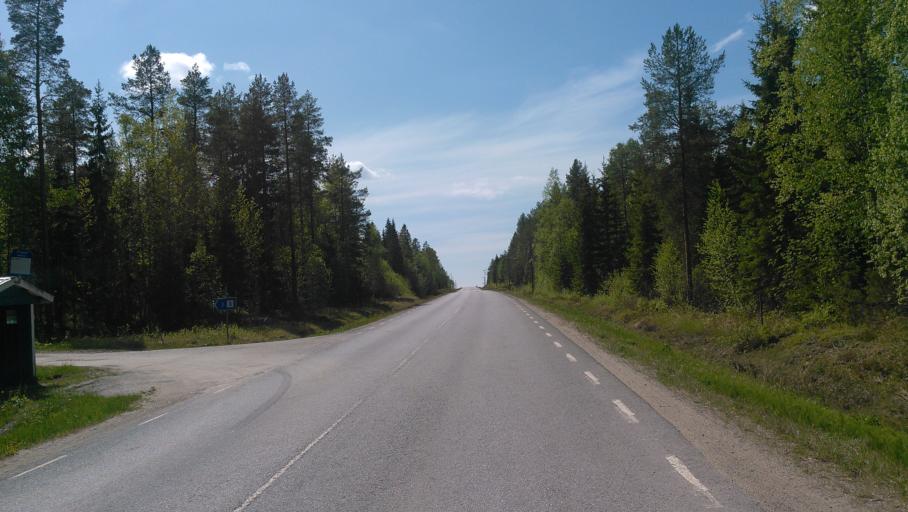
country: SE
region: Vaesterbotten
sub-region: Umea Kommun
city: Roback
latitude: 63.8619
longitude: 20.0095
